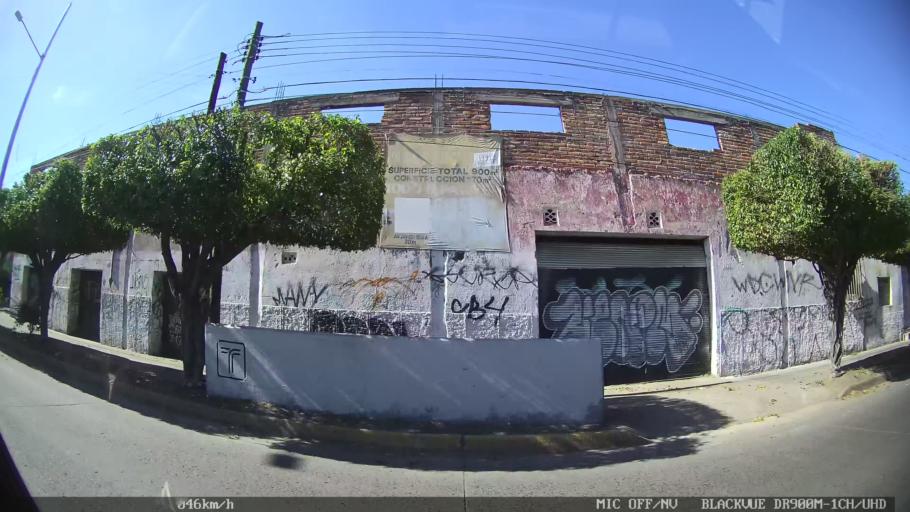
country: MX
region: Jalisco
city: Tlaquepaque
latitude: 20.6654
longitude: -103.3064
